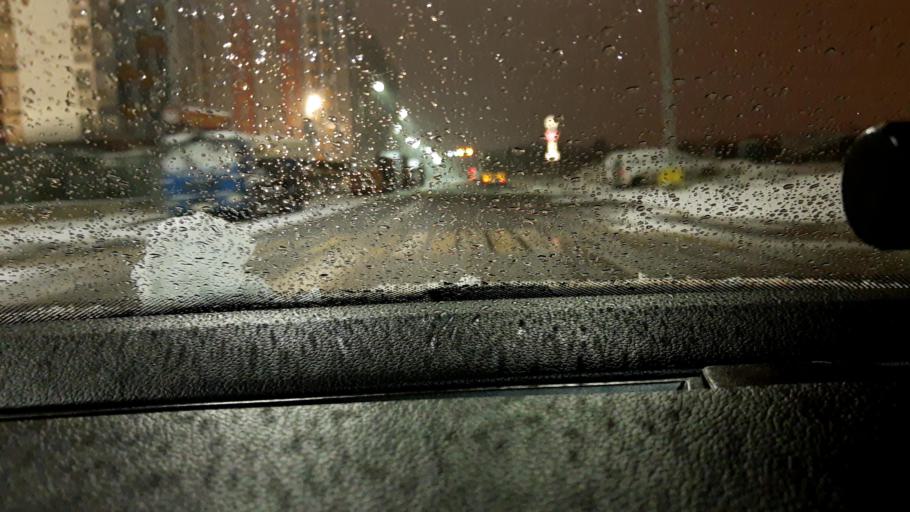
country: RU
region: Moskovskaya
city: Mytishchi
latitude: 55.9276
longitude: 37.7293
